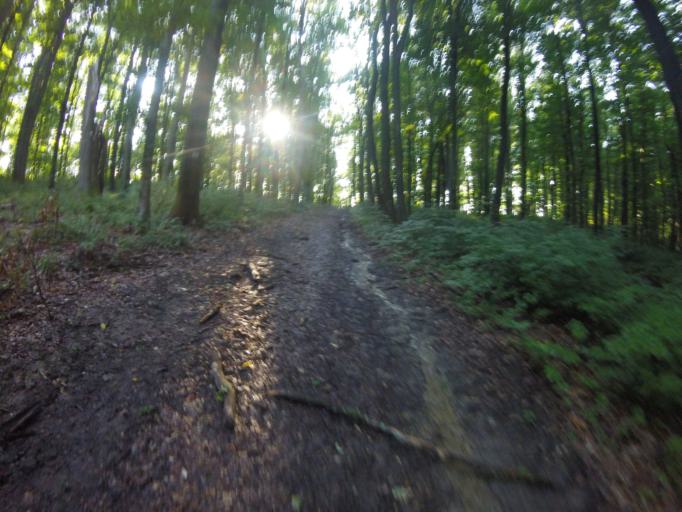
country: HU
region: Zala
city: Letenye
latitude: 46.5145
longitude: 16.7140
